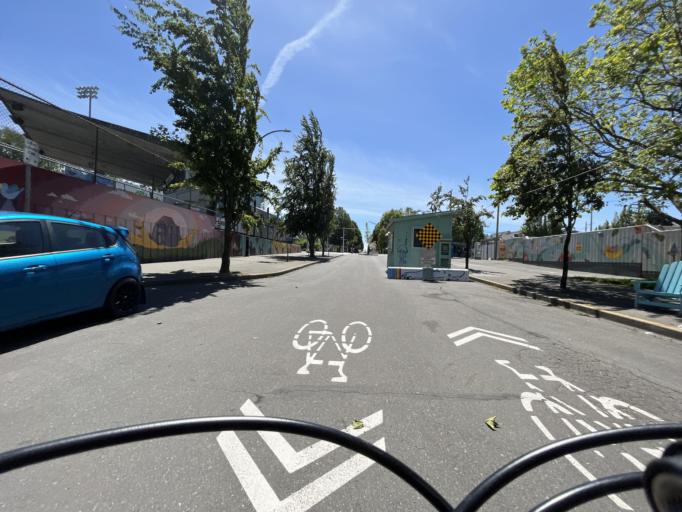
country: CA
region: British Columbia
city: Victoria
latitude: 48.4312
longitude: -123.3557
